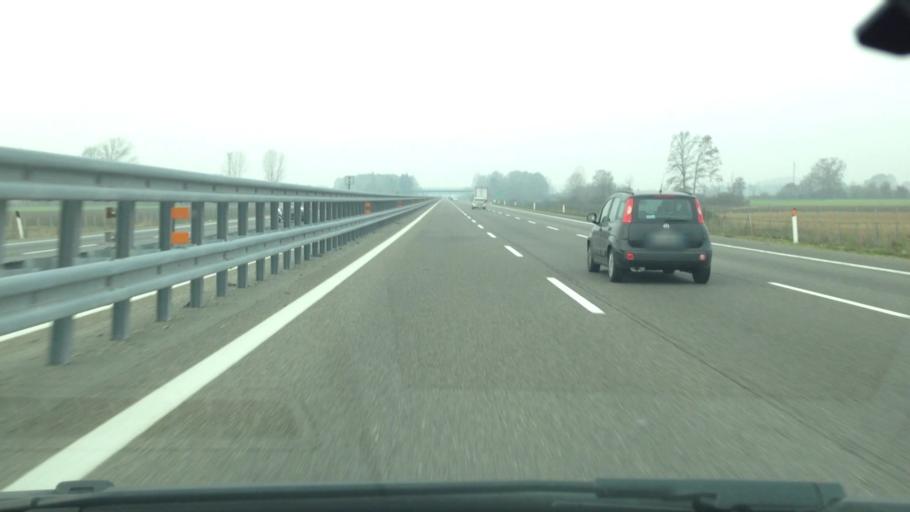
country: IT
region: Piedmont
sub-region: Provincia di Torino
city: Pessione
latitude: 44.9527
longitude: 7.8569
